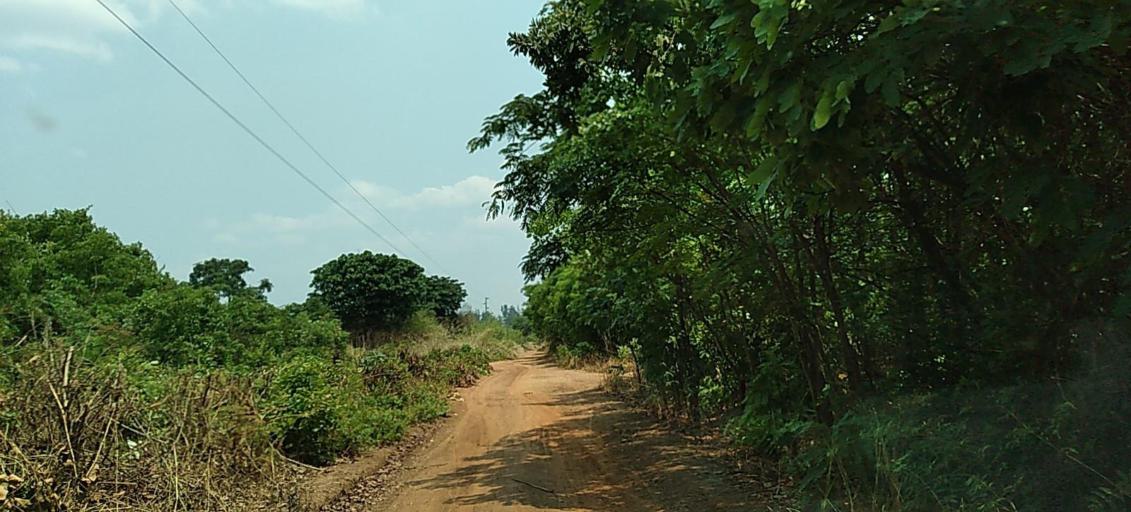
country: ZM
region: Copperbelt
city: Kalulushi
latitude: -12.7630
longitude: 28.0322
